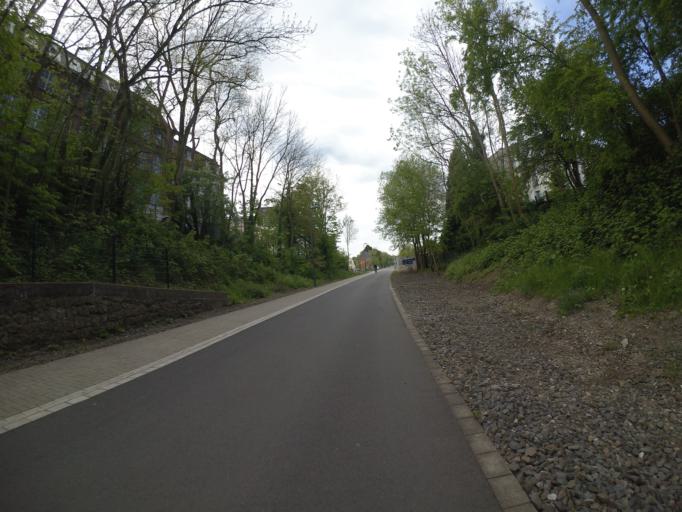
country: DE
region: North Rhine-Westphalia
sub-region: Regierungsbezirk Dusseldorf
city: Wuppertal
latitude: 51.2712
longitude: 7.1843
